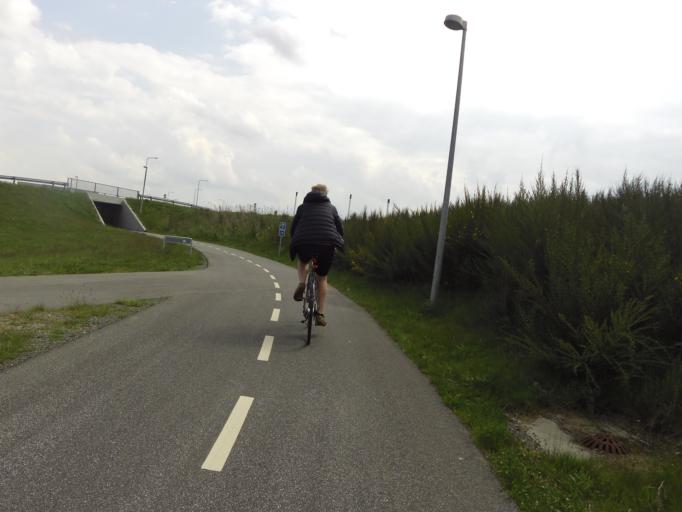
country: DK
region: South Denmark
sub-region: Esbjerg Kommune
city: Esbjerg
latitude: 55.4849
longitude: 8.4170
